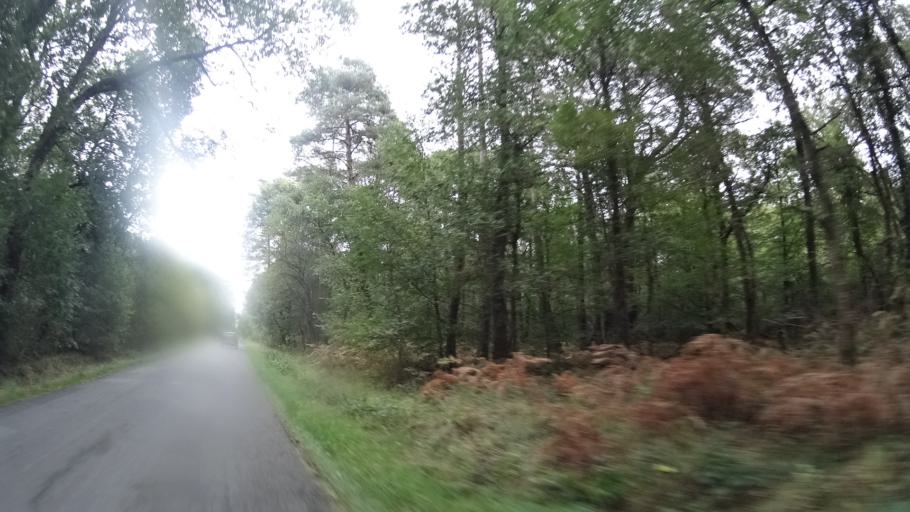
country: FR
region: Brittany
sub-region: Departement d'Ille-et-Vilaine
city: Paimpont
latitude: 48.0794
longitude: -2.1499
